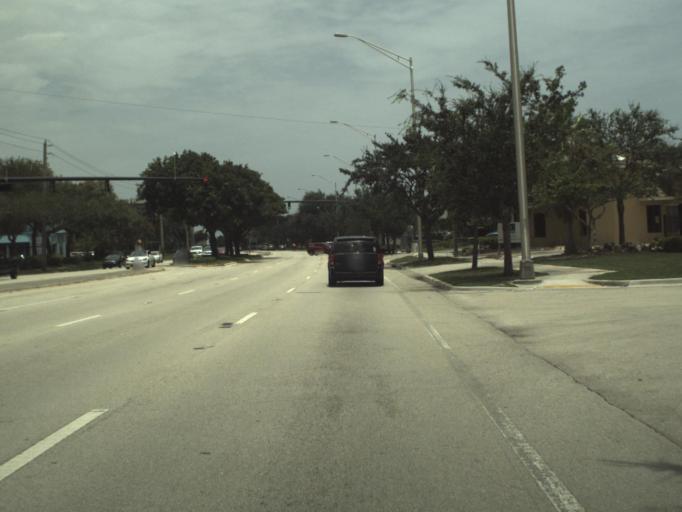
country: US
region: Florida
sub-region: Broward County
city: Lauderdale-by-the-Sea
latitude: 26.1999
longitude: -80.1098
